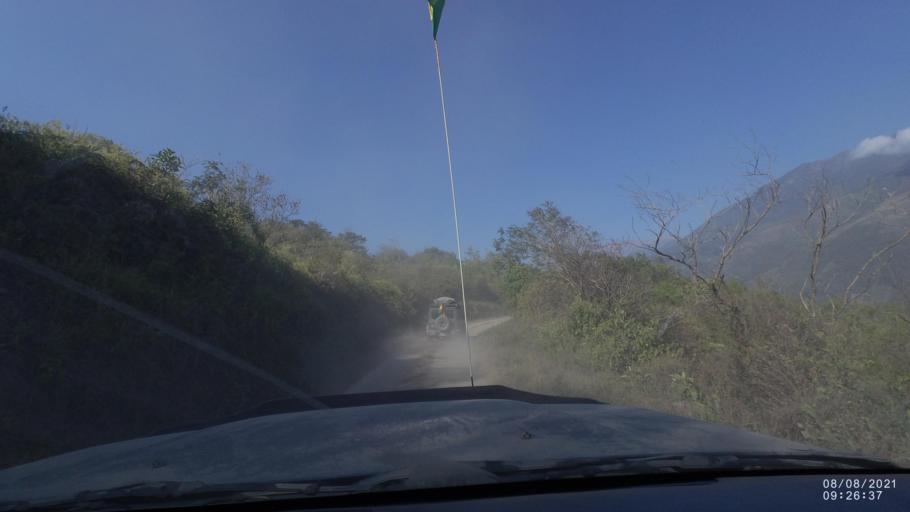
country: BO
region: La Paz
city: Quime
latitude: -16.5884
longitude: -66.7212
